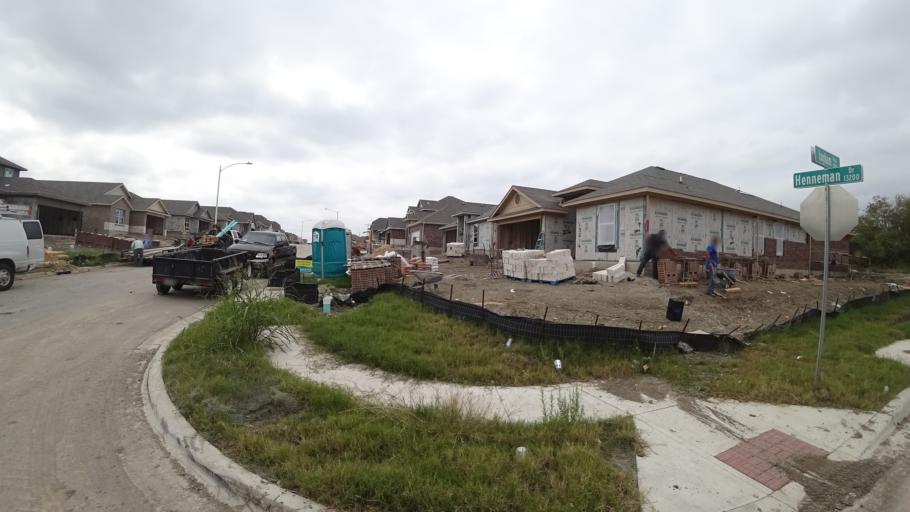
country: US
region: Texas
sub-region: Travis County
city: Pflugerville
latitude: 30.3922
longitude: -97.6223
